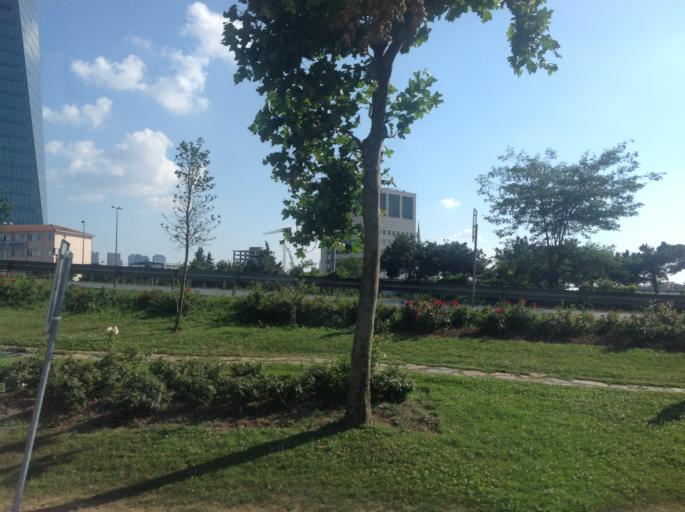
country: TR
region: Istanbul
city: Sisli
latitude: 41.0846
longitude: 29.0089
